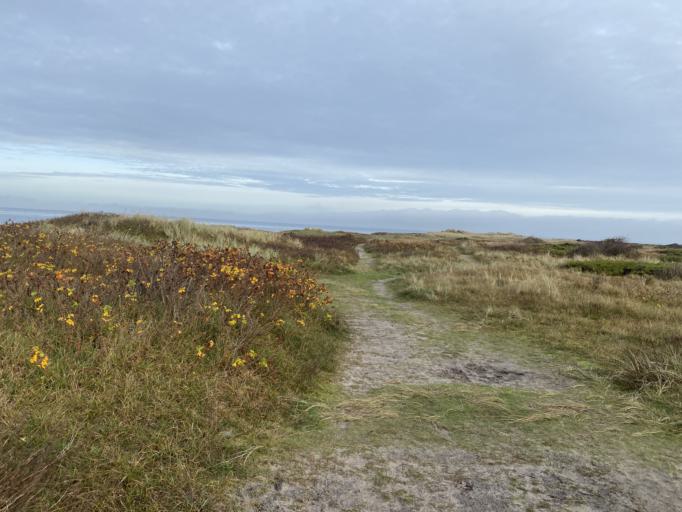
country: DK
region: Capital Region
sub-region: Halsnaes Kommune
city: Hundested
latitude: 55.9752
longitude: 11.7731
